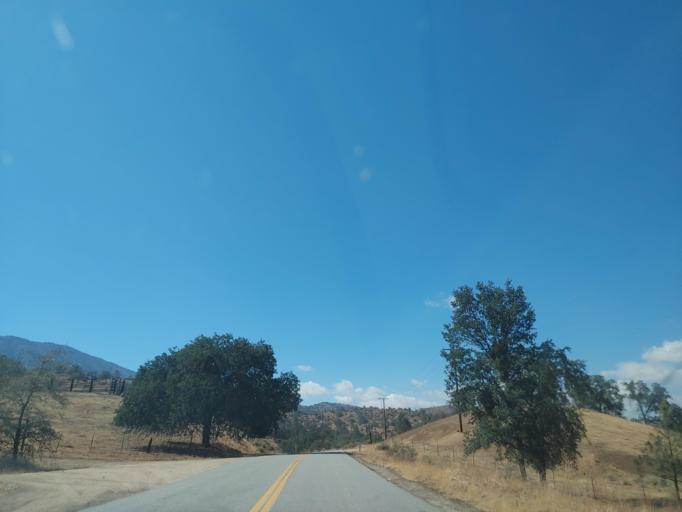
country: US
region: California
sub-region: Kern County
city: Golden Hills
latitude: 35.2063
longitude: -118.5453
